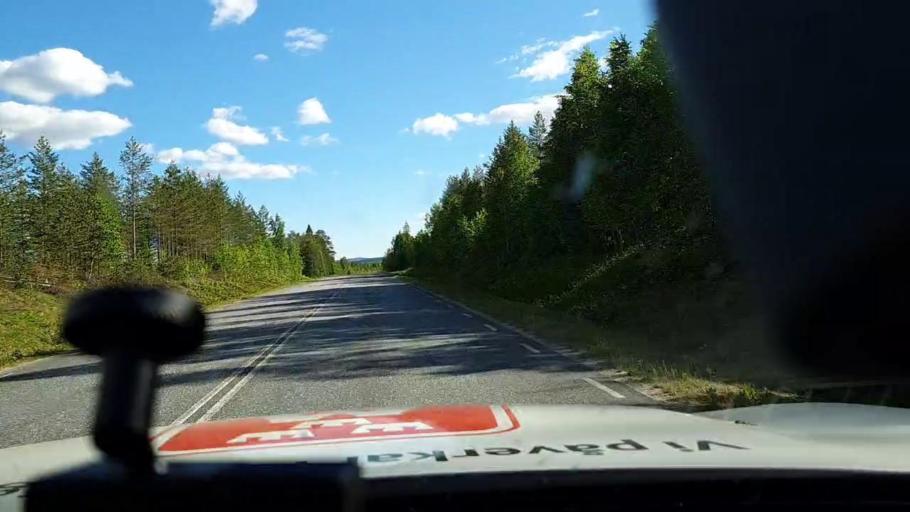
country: SE
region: Norrbotten
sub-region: Overtornea Kommun
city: OEvertornea
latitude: 66.3498
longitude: 23.6479
